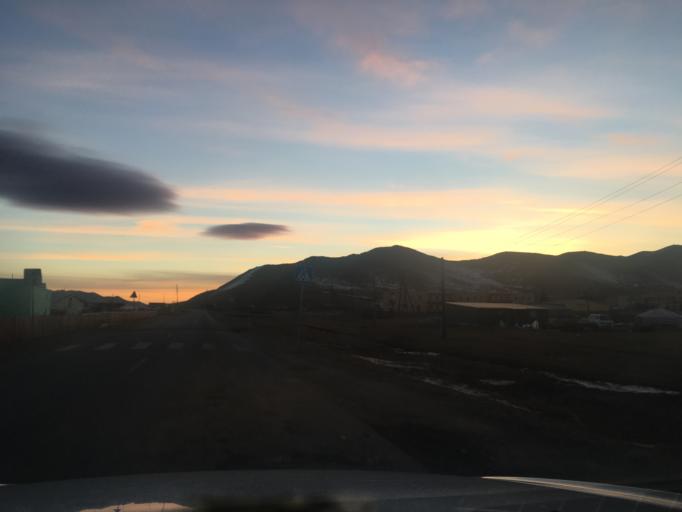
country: MN
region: Central Aimak
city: Mandal
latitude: 48.1229
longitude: 106.6520
